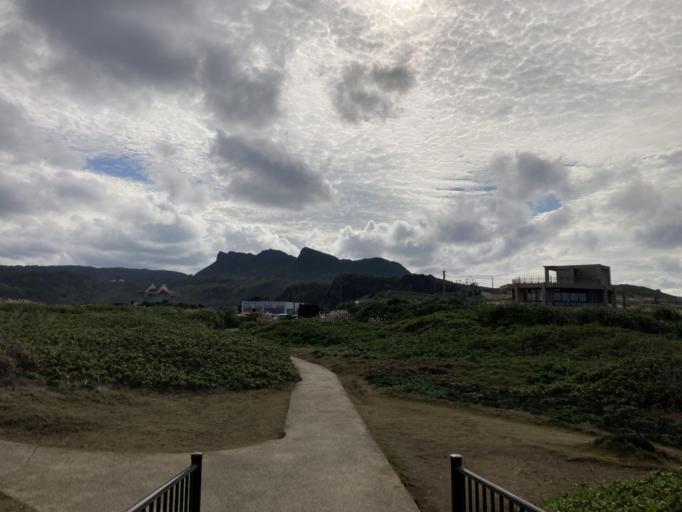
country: JP
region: Okinawa
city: Nago
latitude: 26.8732
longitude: 128.2641
